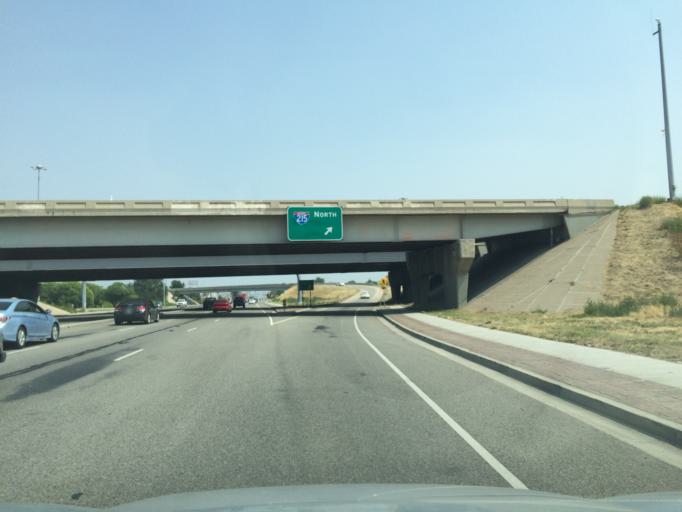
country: US
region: Utah
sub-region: Salt Lake County
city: Taylorsville
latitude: 40.6966
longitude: -111.9534
